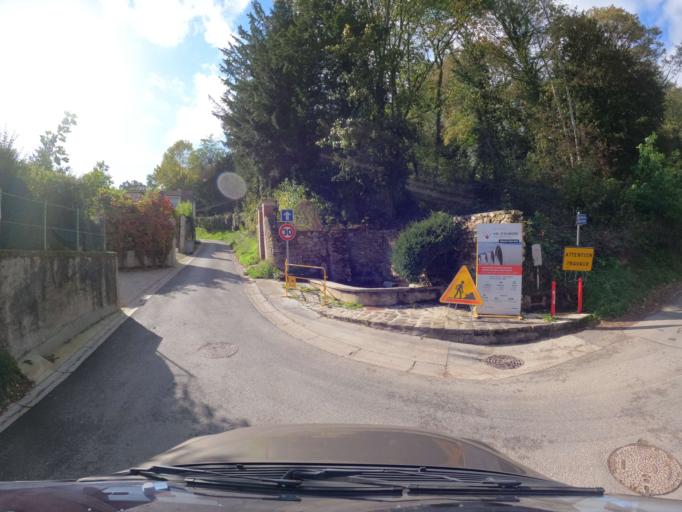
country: FR
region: Ile-de-France
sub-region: Departement de Seine-et-Marne
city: Montry
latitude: 48.8871
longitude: 2.8220
